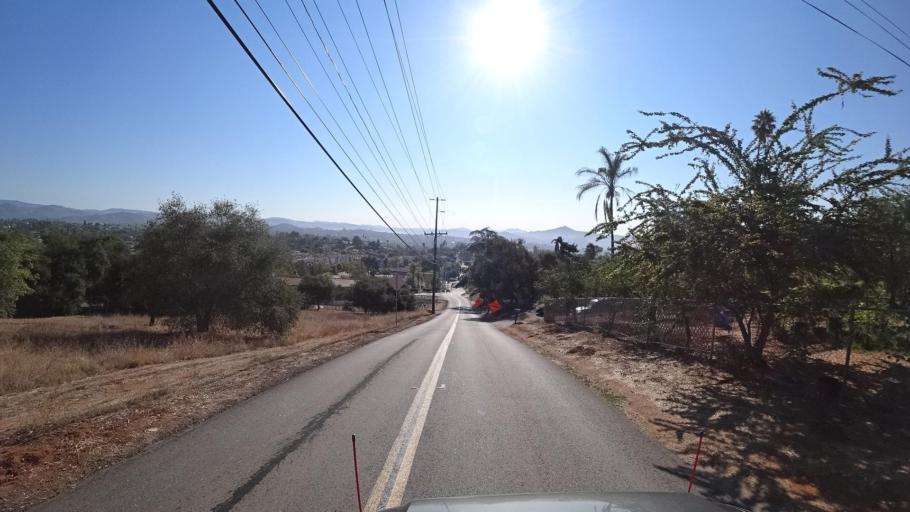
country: US
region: California
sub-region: San Diego County
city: Escondido
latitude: 33.0913
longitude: -117.0753
